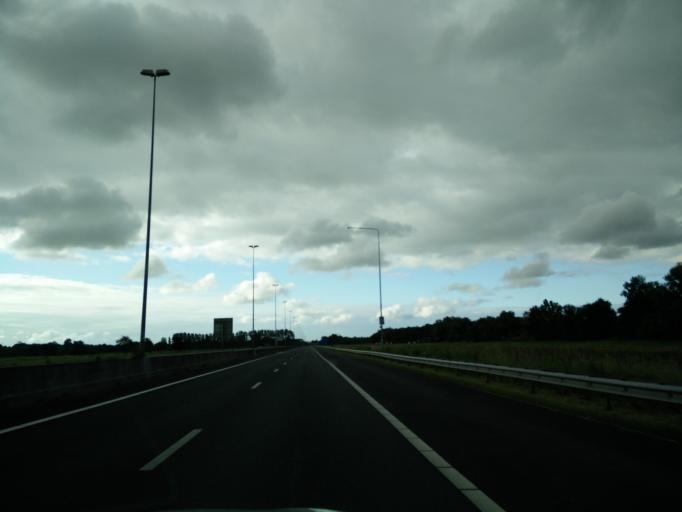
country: NL
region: Groningen
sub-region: Gemeente Haren
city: Haren
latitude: 53.1797
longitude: 6.5798
